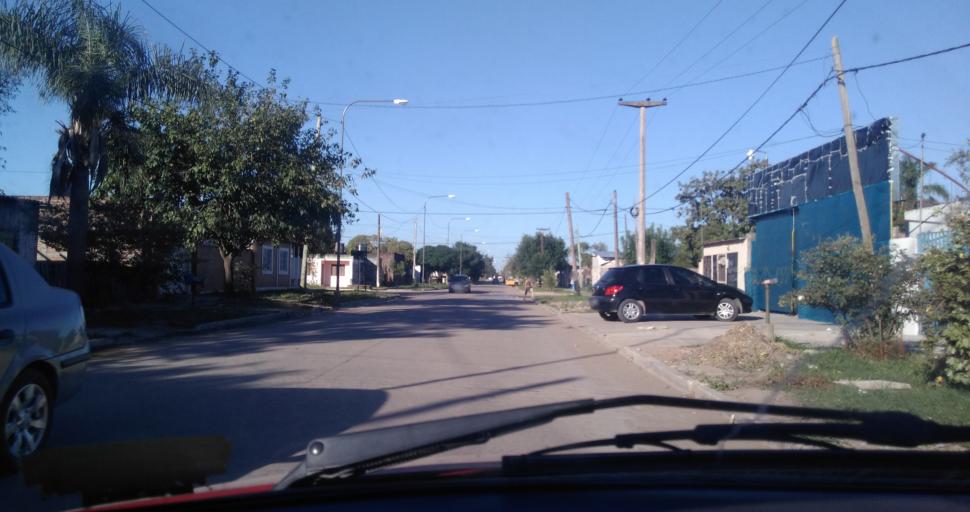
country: AR
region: Chaco
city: Resistencia
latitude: -27.4787
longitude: -58.9678
